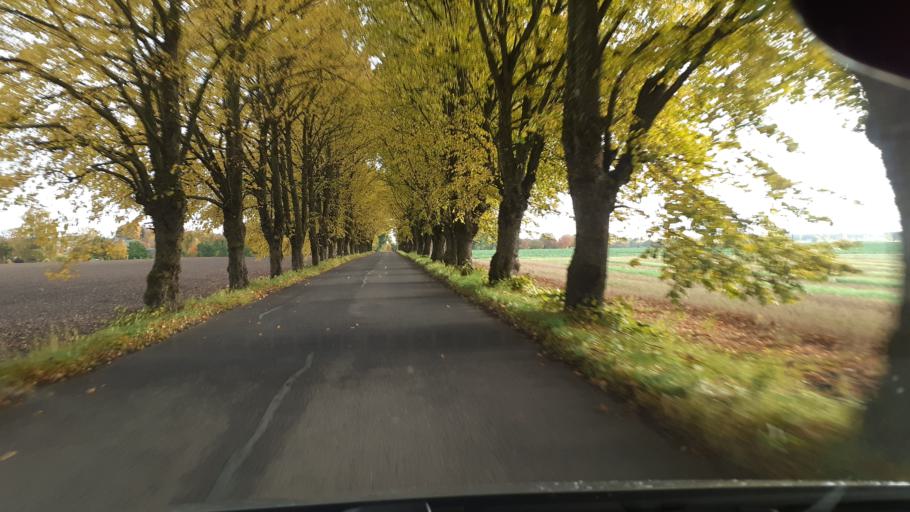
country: LV
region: Kuldigas Rajons
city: Kuldiga
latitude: 57.0116
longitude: 21.9009
